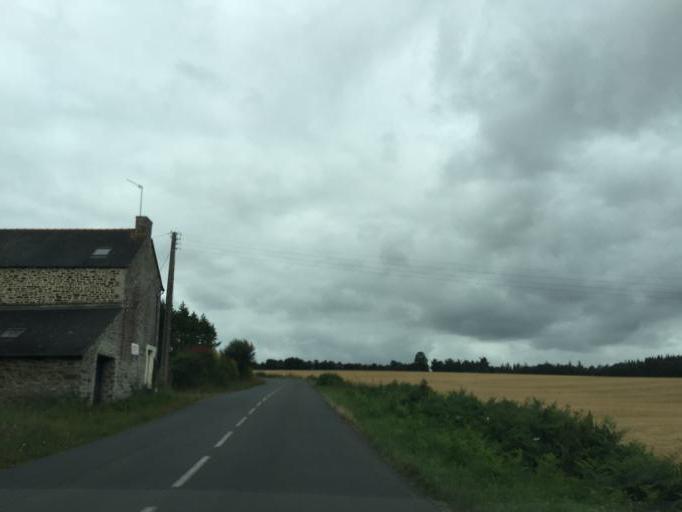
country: FR
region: Brittany
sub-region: Departement des Cotes-d'Armor
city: Jugon-les-Lacs
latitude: 48.3926
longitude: -2.3417
